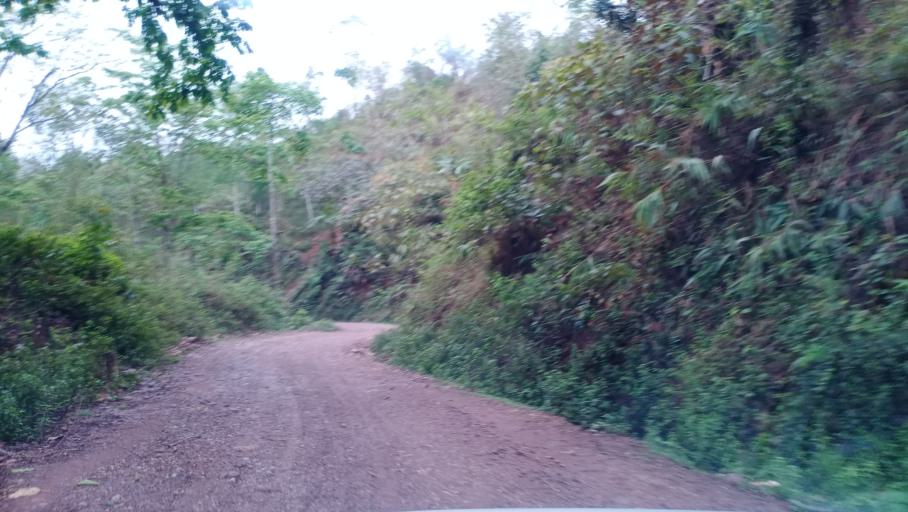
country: LA
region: Phongsali
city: Phongsali
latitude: 21.3397
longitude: 102.0760
